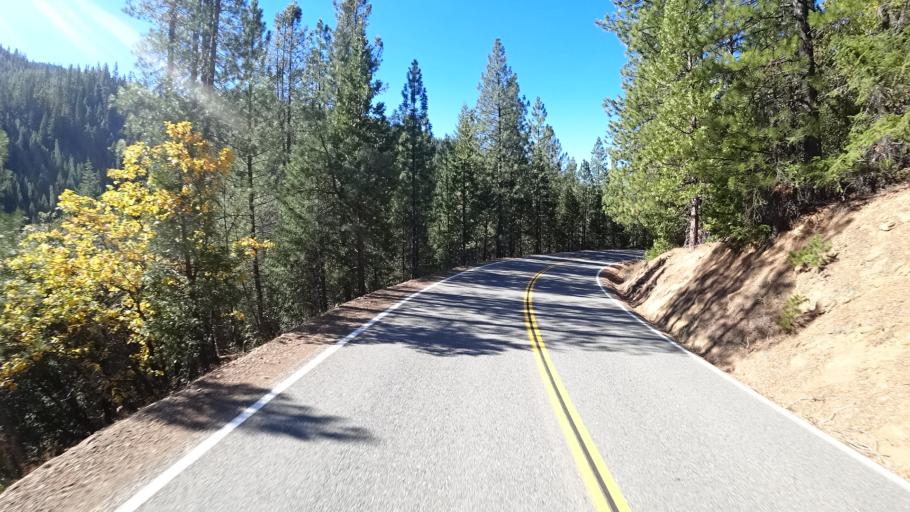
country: US
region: California
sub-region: Trinity County
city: Weaverville
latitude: 41.2205
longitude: -123.0103
